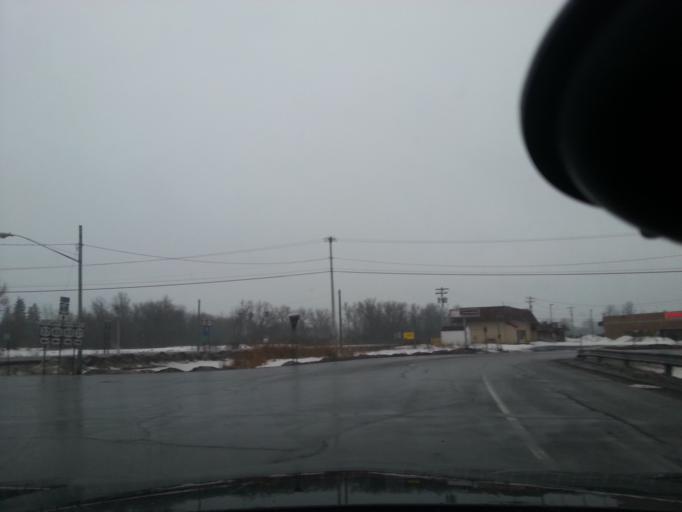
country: US
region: New York
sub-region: St. Lawrence County
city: Ogdensburg
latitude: 44.6904
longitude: -75.4756
